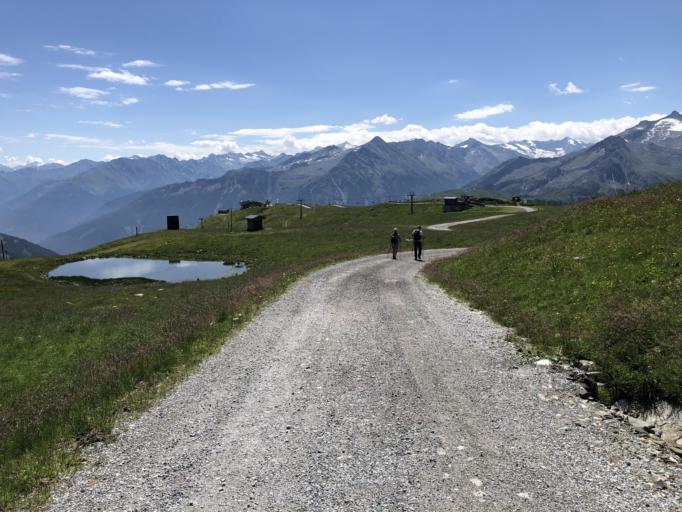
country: AT
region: Salzburg
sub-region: Politischer Bezirk Zell am See
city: Krimml
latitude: 47.2610
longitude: 12.0942
